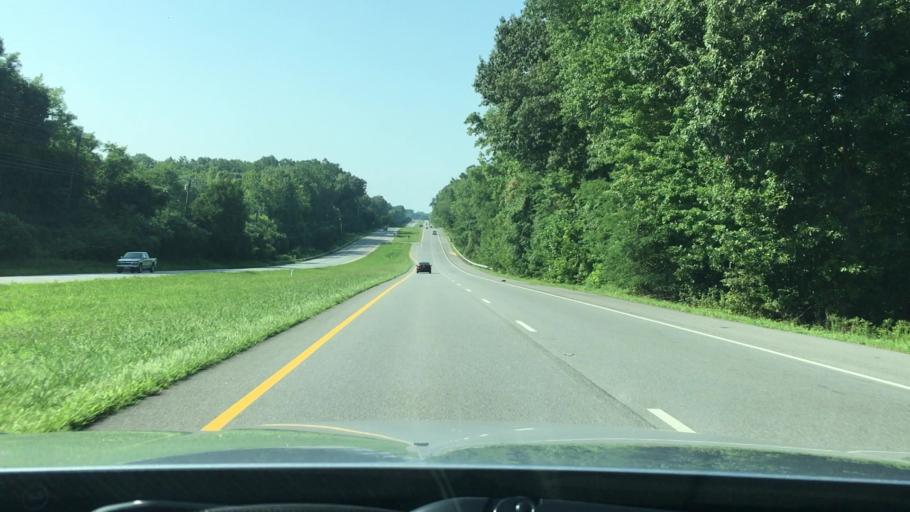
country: US
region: Virginia
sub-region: King George County
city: Dahlgren
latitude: 38.3966
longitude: -76.9538
